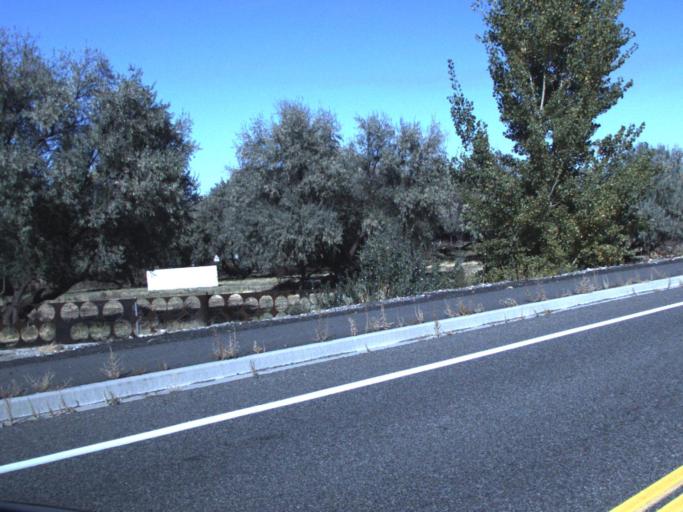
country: US
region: Washington
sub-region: Benton County
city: Finley
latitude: 46.1389
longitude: -119.0313
